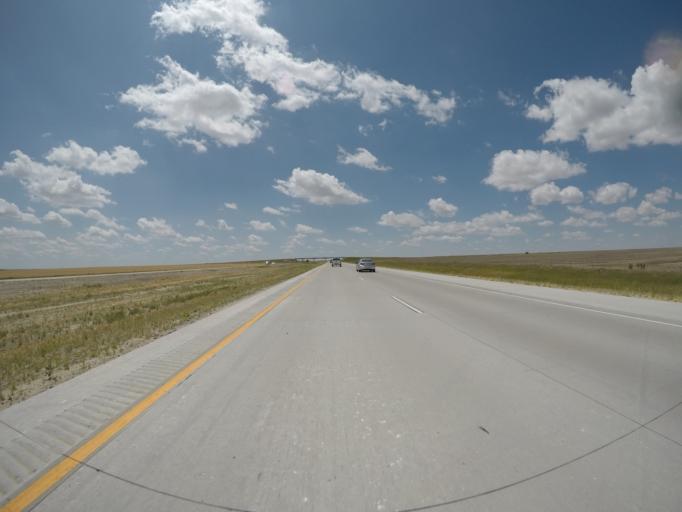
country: US
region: Colorado
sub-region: Kit Carson County
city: Burlington
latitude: 39.2942
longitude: -102.7753
